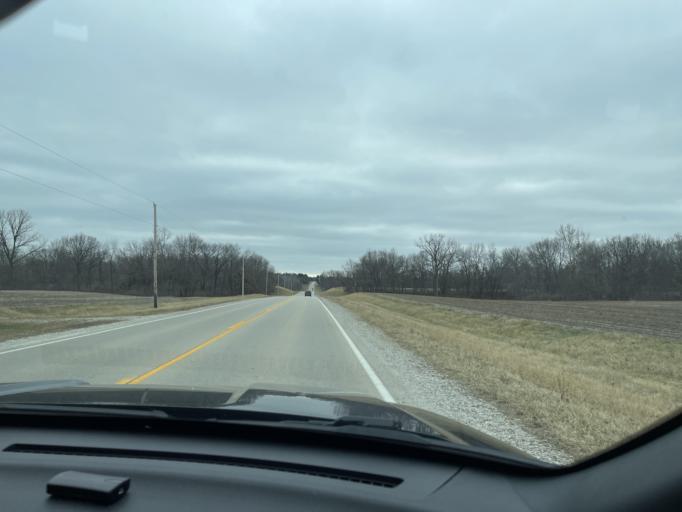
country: US
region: Illinois
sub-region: Sangamon County
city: Leland Grove
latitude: 39.8163
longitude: -89.7396
